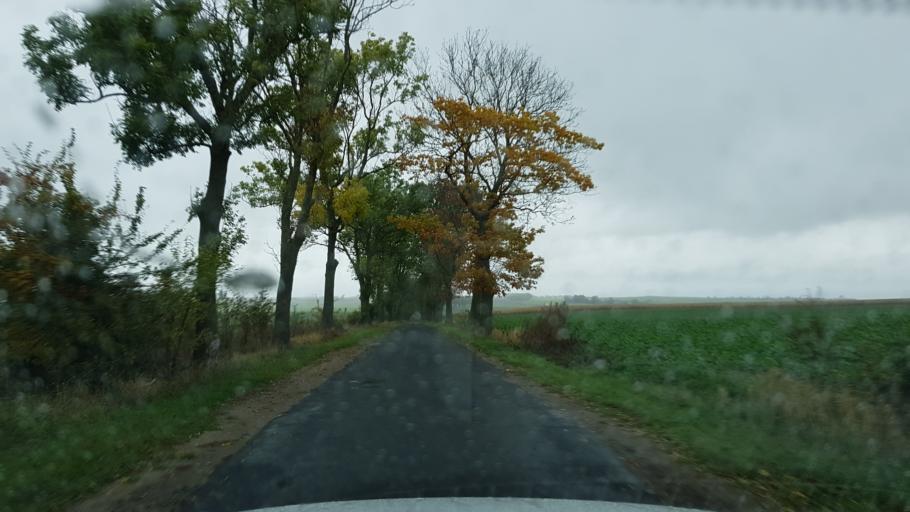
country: PL
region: West Pomeranian Voivodeship
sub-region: Powiat pyrzycki
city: Kozielice
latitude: 53.0370
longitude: 14.8543
